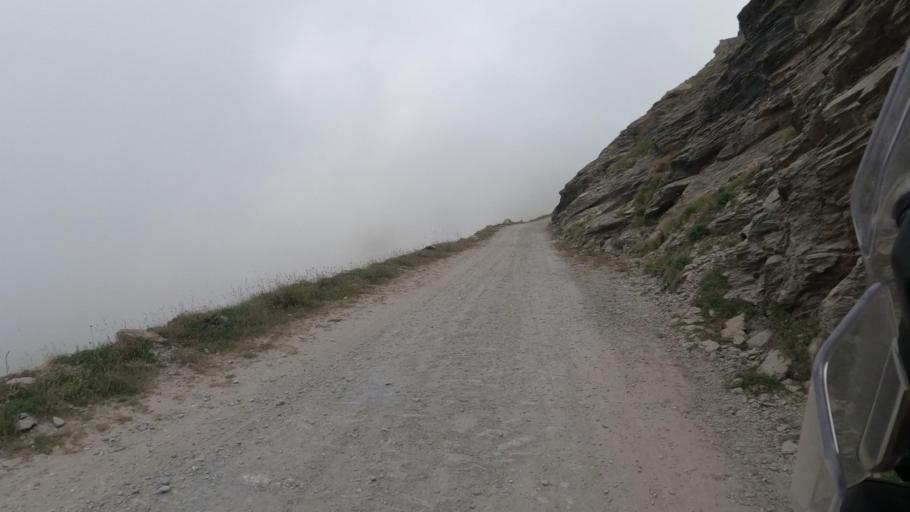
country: IT
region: Piedmont
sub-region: Provincia di Torino
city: Exilles
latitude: 45.0606
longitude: 6.9679
